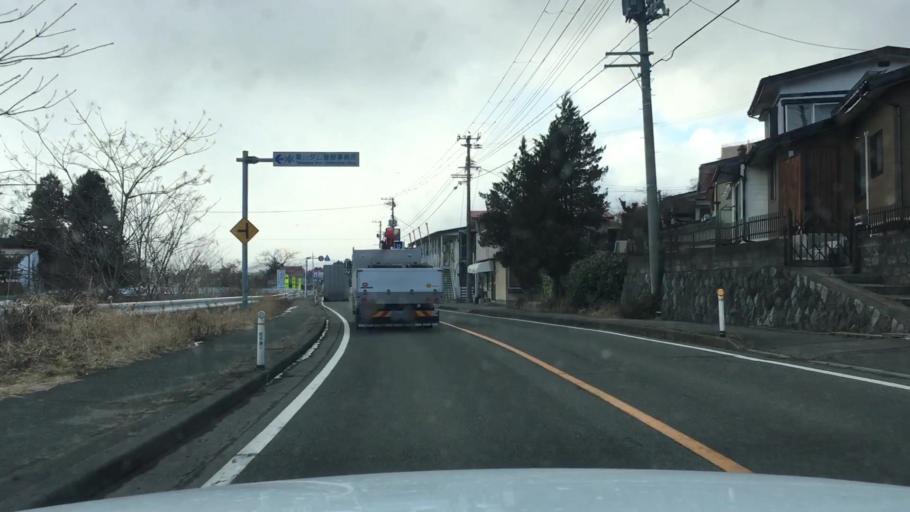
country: JP
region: Iwate
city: Morioka-shi
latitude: 39.6872
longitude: 141.1807
